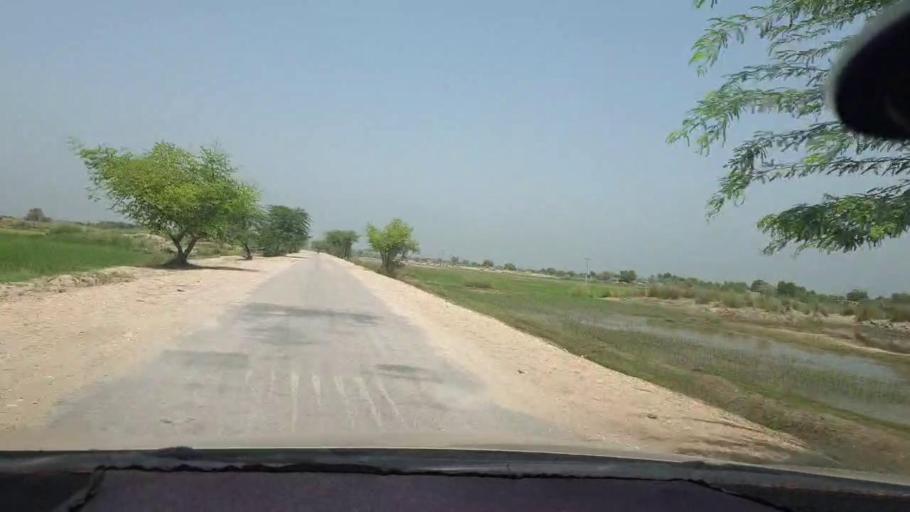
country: PK
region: Sindh
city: Kambar
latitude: 27.6714
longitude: 67.9125
